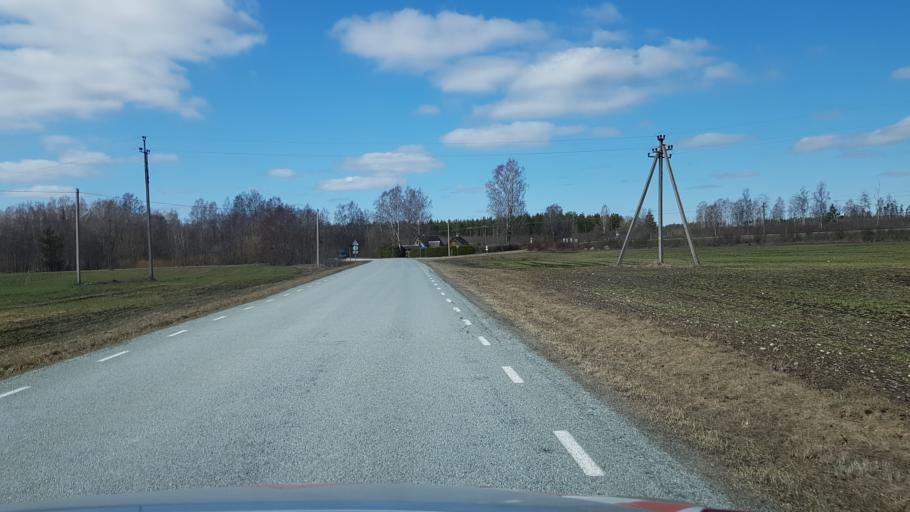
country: EE
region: Laeaene-Virumaa
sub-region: Tapa vald
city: Tapa
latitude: 59.2523
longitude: 25.7389
